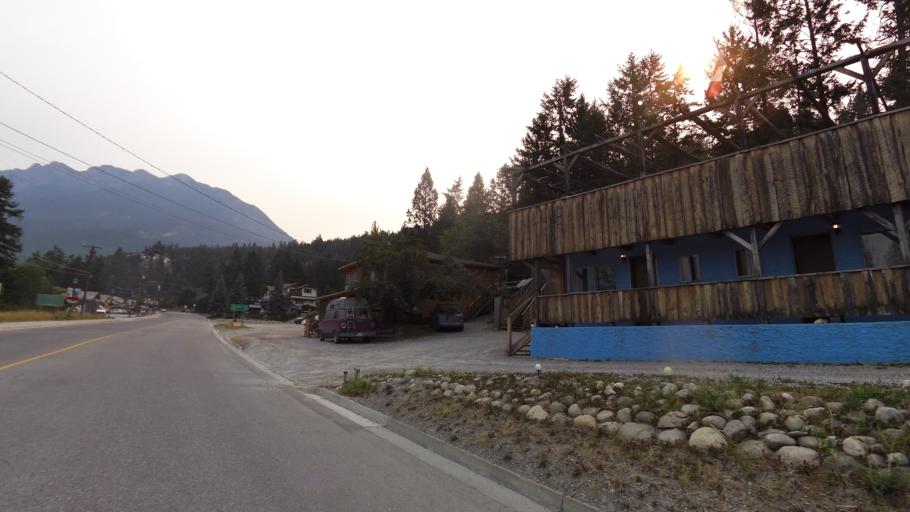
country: CA
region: British Columbia
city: Invermere
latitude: 50.6240
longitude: -116.0694
